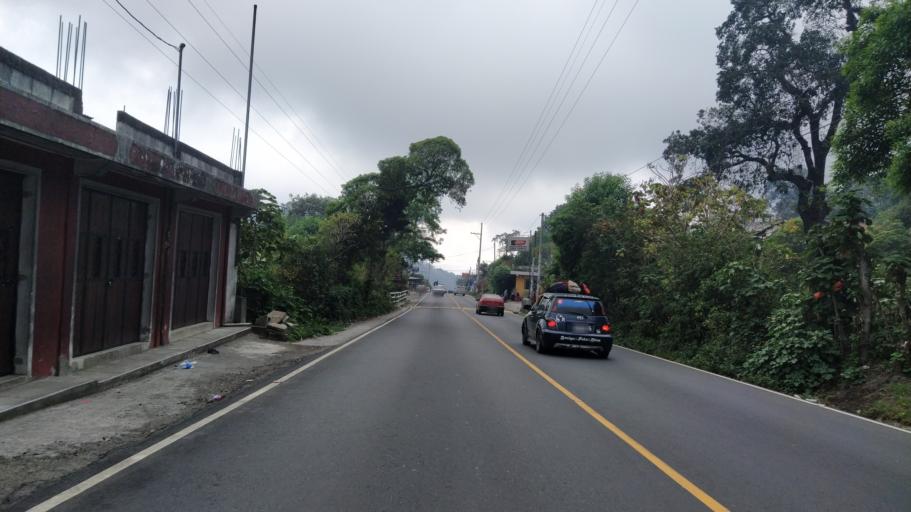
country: GT
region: Suchitepeque
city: Pueblo Nuevo
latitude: 14.7235
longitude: -91.5269
